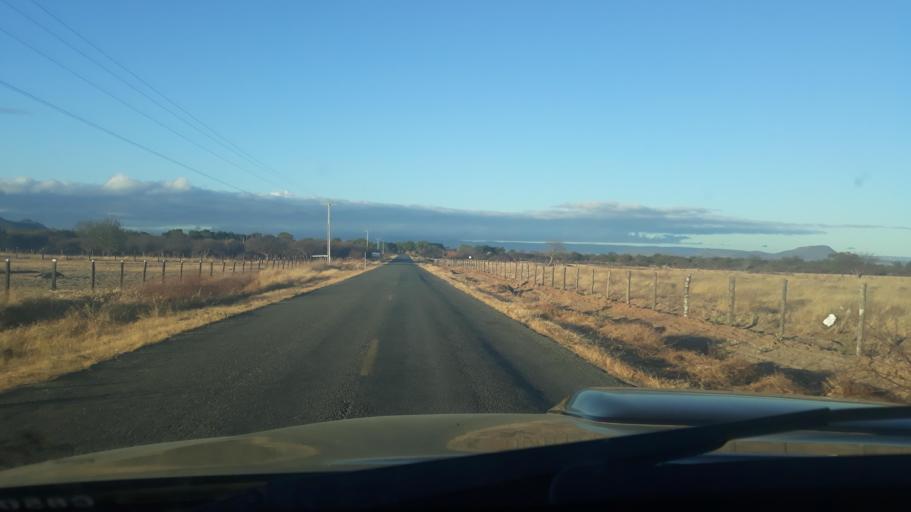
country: BR
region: Bahia
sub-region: Guanambi
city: Guanambi
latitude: -14.0679
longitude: -42.8785
